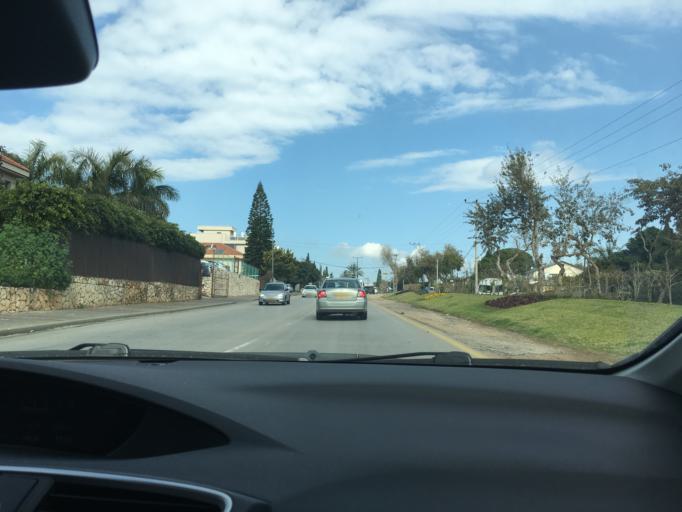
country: IL
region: Tel Aviv
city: Ramat HaSharon
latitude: 32.1660
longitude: 34.8530
